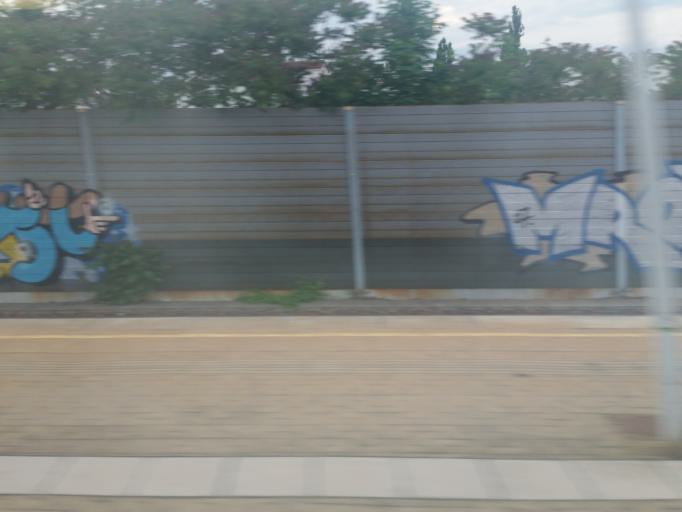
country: AT
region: Lower Austria
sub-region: Politischer Bezirk Wien-Umgebung
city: Leopoldsdorf
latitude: 48.1688
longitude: 16.4175
